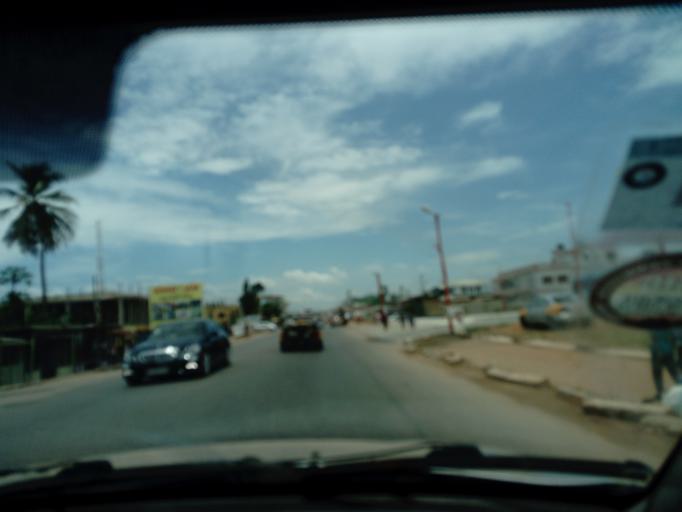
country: GH
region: Central
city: Cape Coast
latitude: 5.1294
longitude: -1.2745
